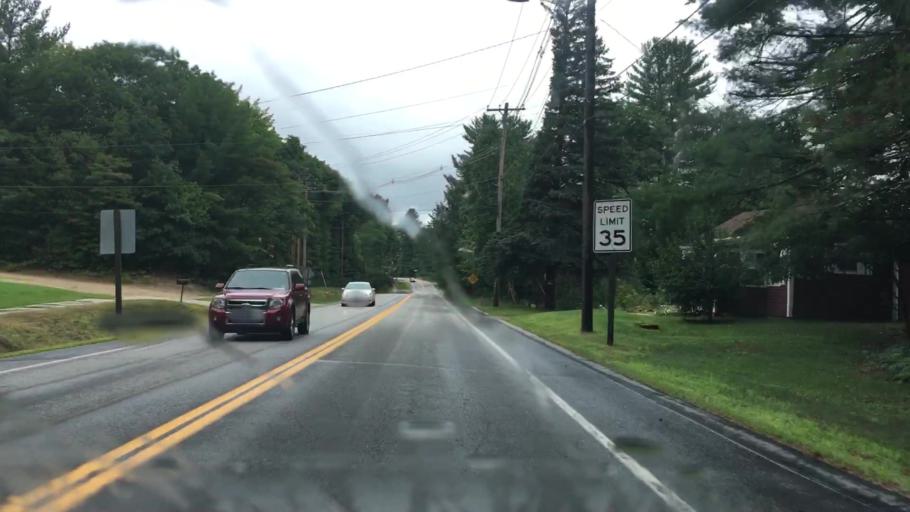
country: US
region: Maine
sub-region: Oxford County
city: Fryeburg
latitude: 44.0136
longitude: -70.9731
